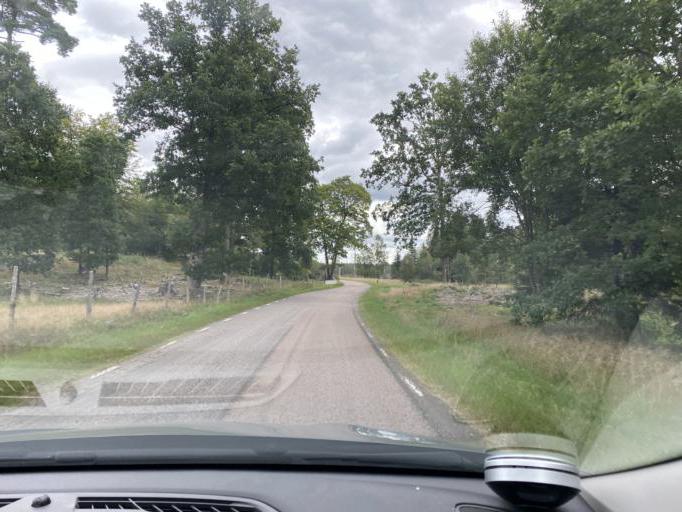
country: SE
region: Kronoberg
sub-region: Markaryds Kommun
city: Markaryd
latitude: 56.4880
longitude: 13.5466
